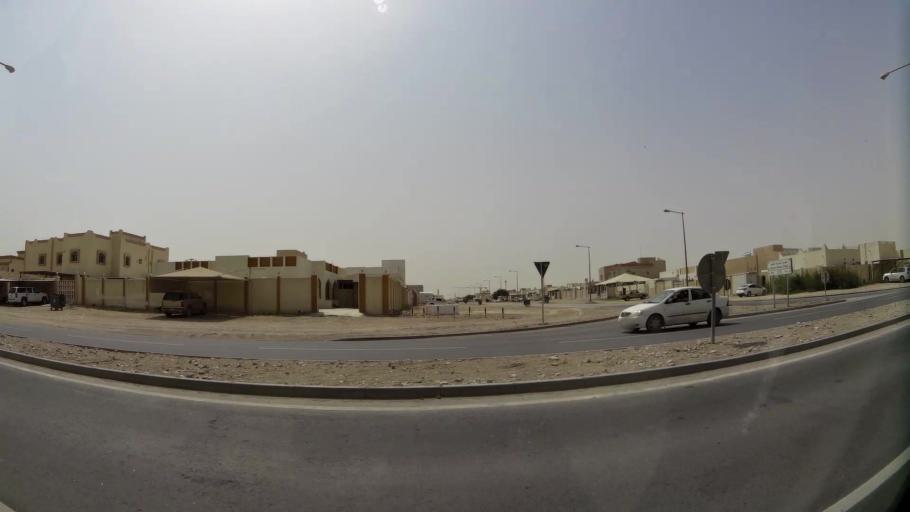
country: QA
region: Baladiyat ar Rayyan
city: Ar Rayyan
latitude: 25.2407
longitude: 51.3797
